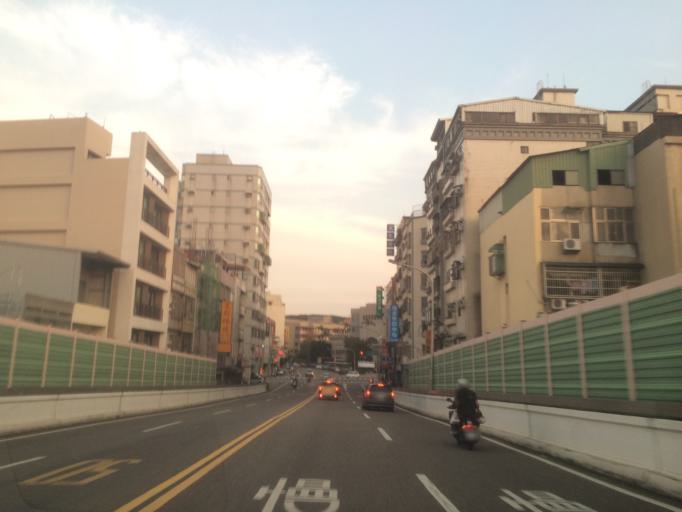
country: TW
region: Taiwan
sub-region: Hsinchu
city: Hsinchu
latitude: 24.7958
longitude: 120.9645
